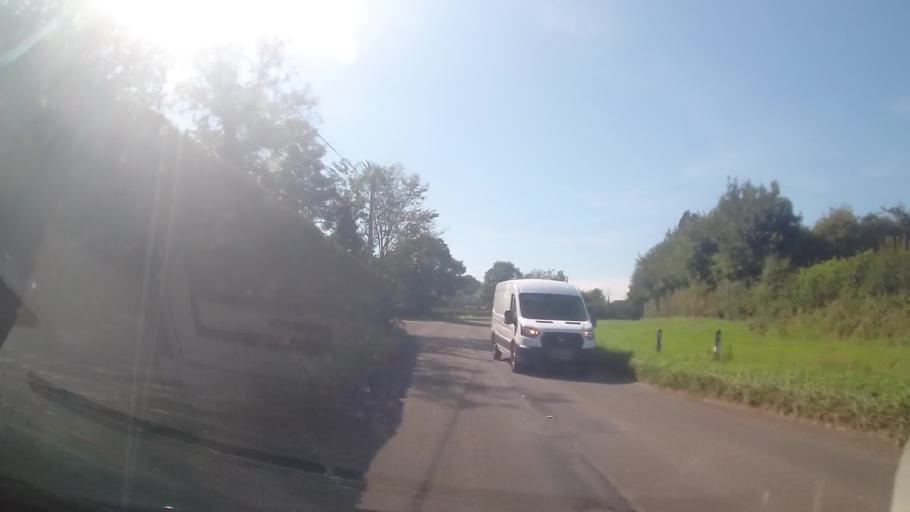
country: GB
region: Wales
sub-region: Sir Powys
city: Montgomery
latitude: 52.5324
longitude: -3.1038
